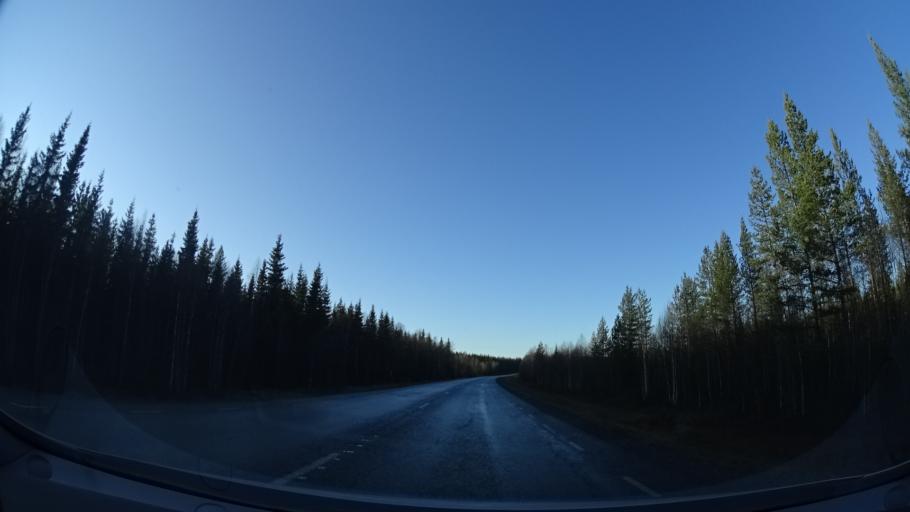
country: SE
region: Vaesterbotten
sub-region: Skelleftea Kommun
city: Langsele
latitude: 64.8846
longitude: 20.2044
